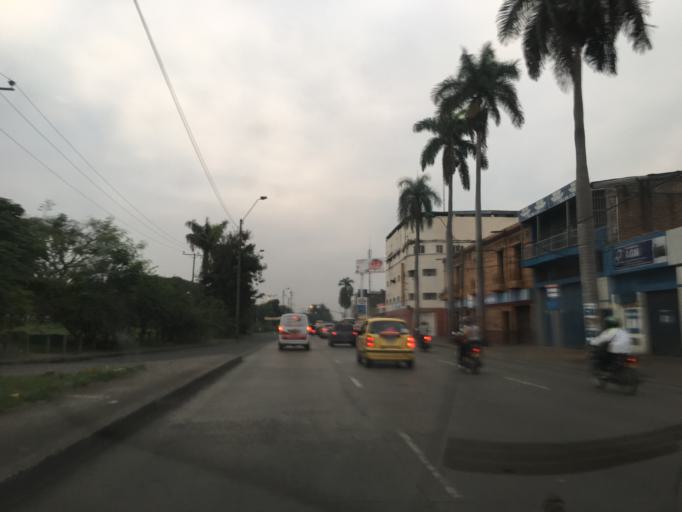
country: CO
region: Valle del Cauca
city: Cali
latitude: 3.4543
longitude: -76.5195
